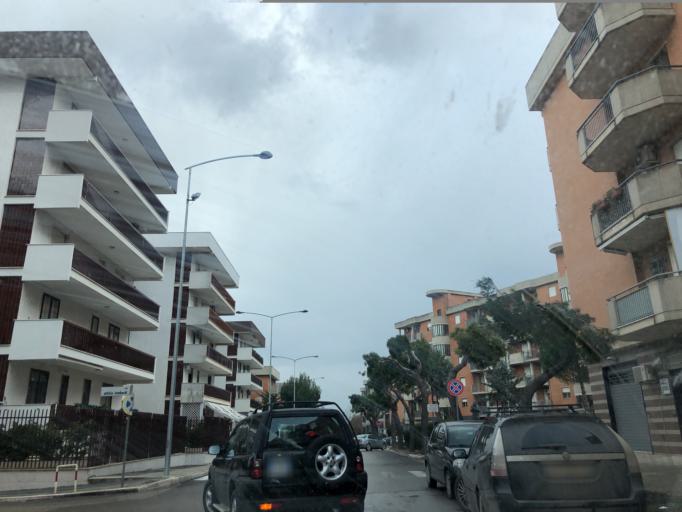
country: IT
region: Apulia
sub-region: Provincia di Foggia
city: Lucera
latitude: 41.5014
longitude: 15.3465
